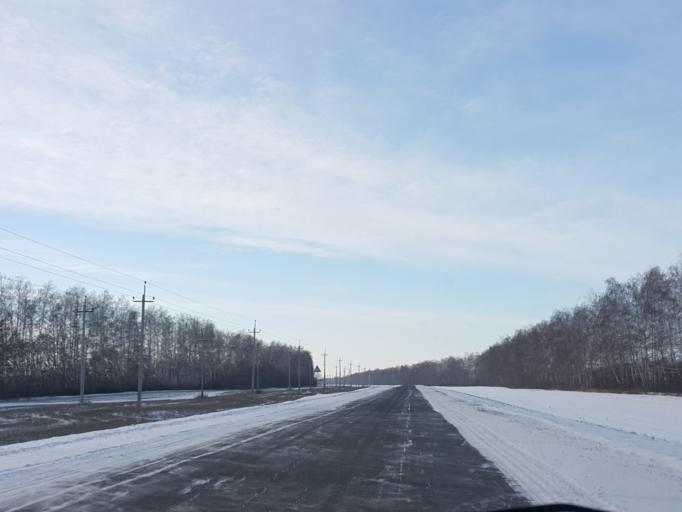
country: RU
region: Tambov
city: Znamenka
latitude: 52.3930
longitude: 41.3586
